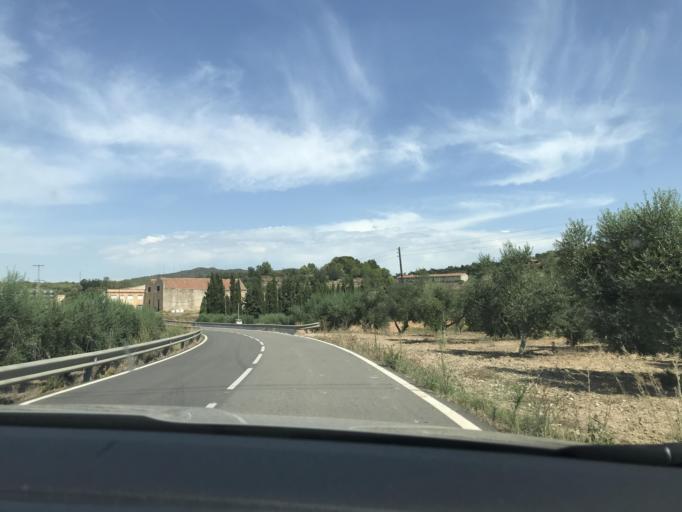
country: ES
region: Catalonia
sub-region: Provincia de Tarragona
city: Salomo
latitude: 41.2224
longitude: 1.3783
